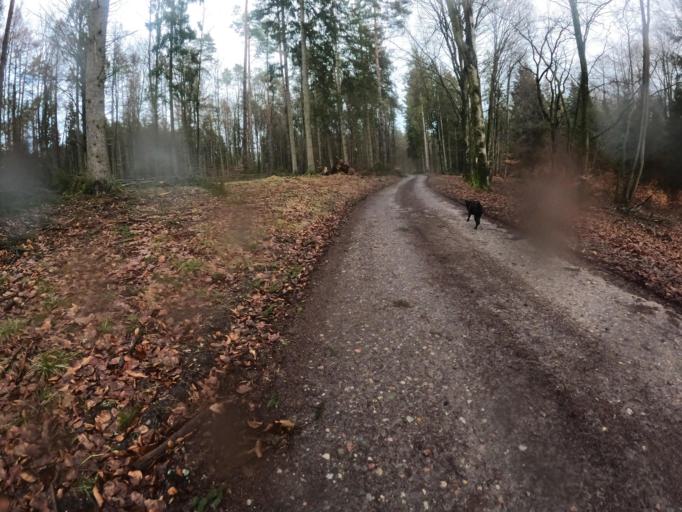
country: PL
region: West Pomeranian Voivodeship
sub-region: Powiat slawienski
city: Slawno
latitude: 54.2585
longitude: 16.7001
